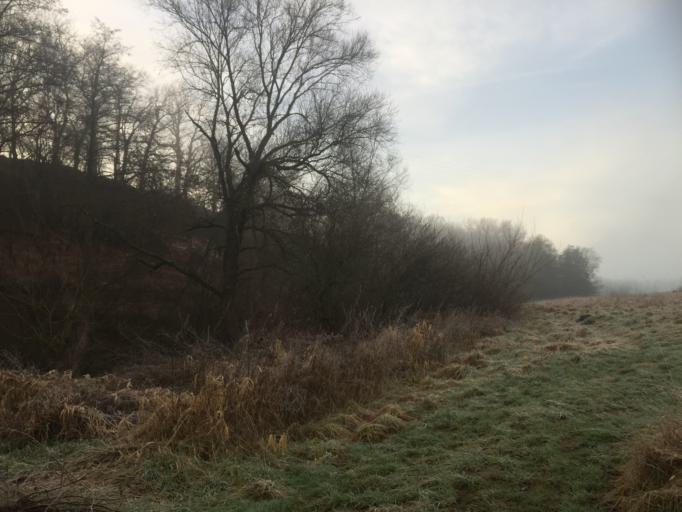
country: DE
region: Thuringia
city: Orlamunde
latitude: 50.7720
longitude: 11.5326
